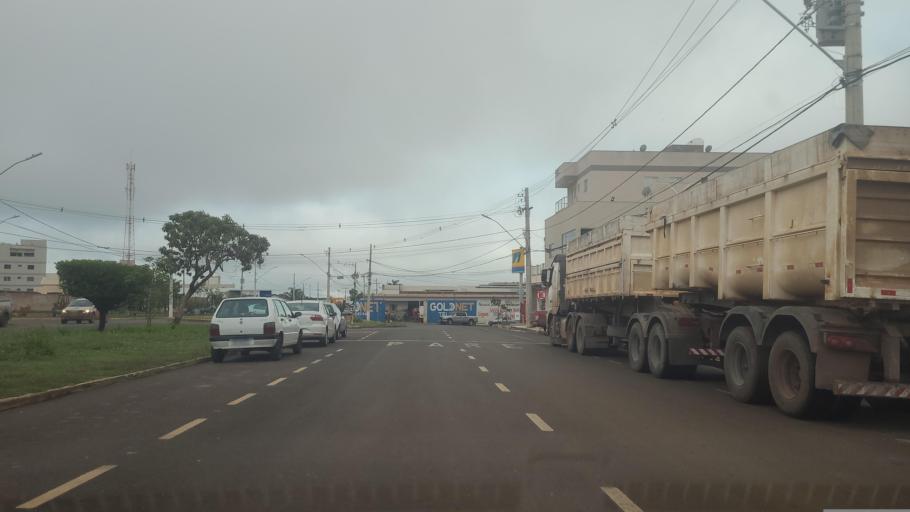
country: BR
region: Minas Gerais
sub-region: Carmo Do Paranaiba
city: Carmo do Paranaiba
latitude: -19.1999
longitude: -46.2352
